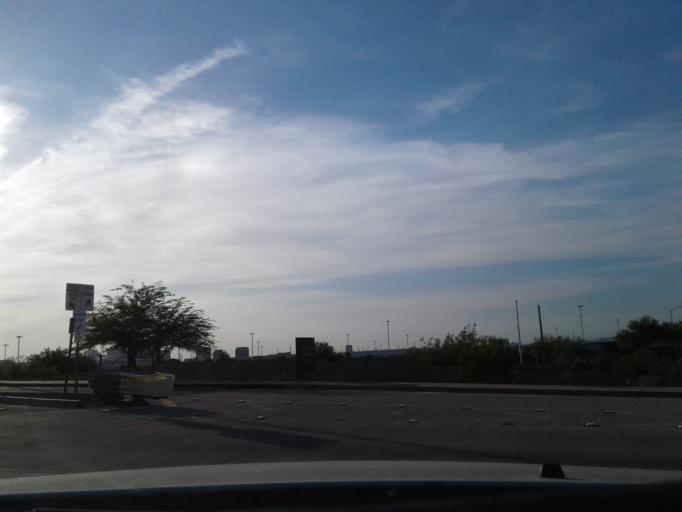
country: US
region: Arizona
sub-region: Maricopa County
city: Phoenix
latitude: 33.4318
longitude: -112.0433
